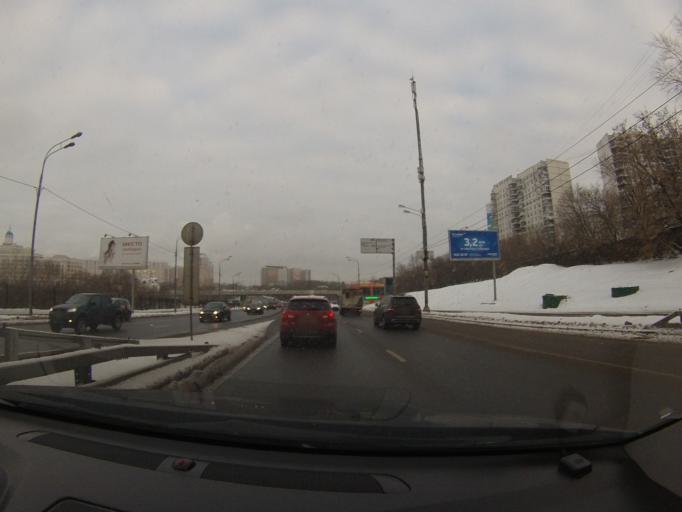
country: RU
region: Moscow
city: Nikol'skoye
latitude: 55.6836
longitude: 37.4799
